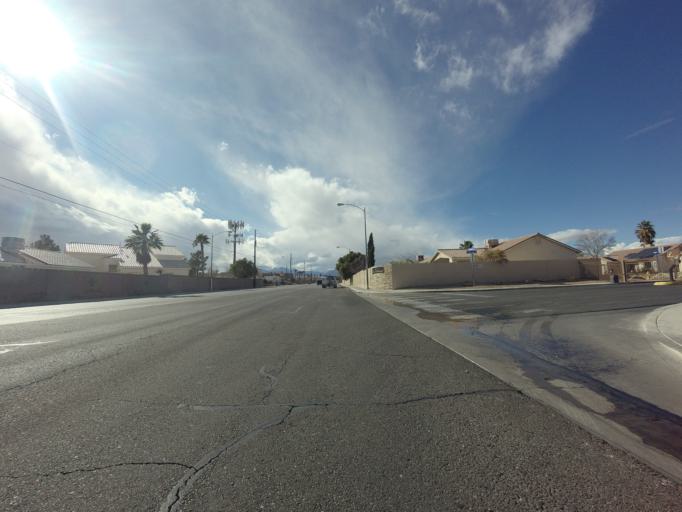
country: US
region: Nevada
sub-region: Clark County
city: North Las Vegas
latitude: 36.2544
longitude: -115.1506
